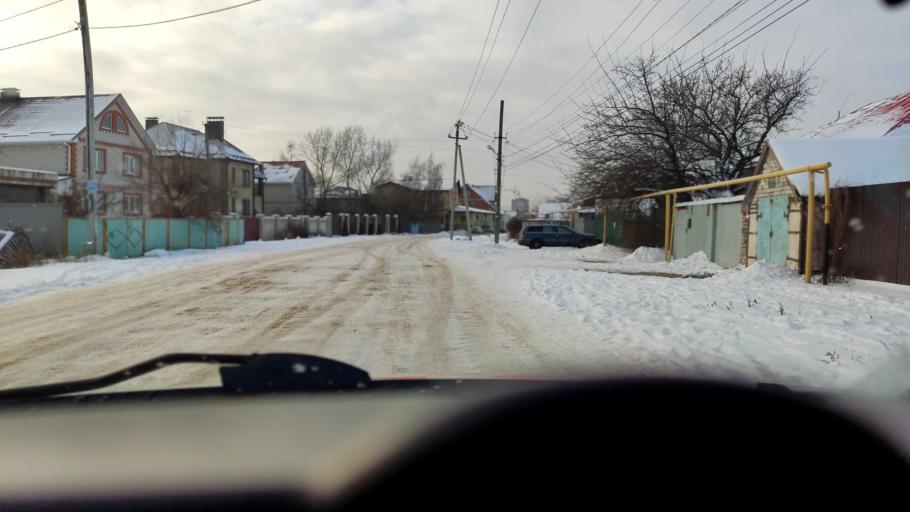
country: RU
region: Voronezj
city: Podgornoye
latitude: 51.7270
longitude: 39.1573
